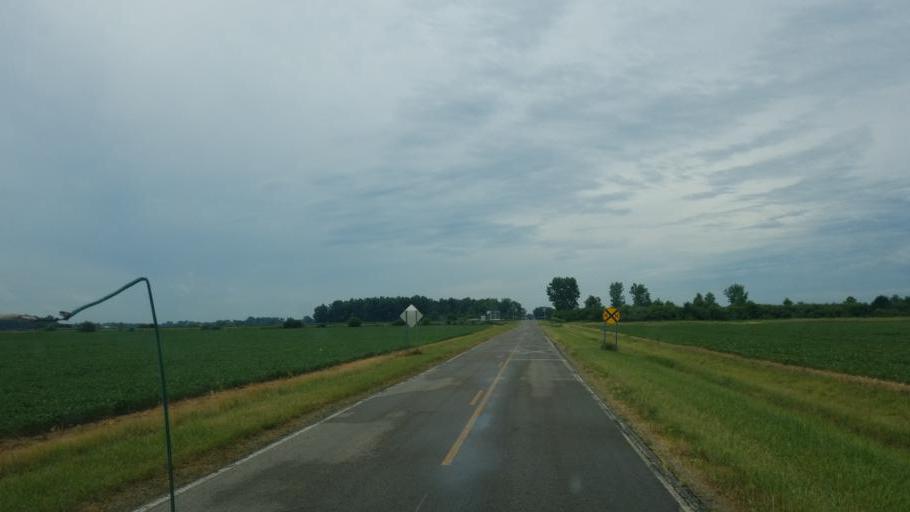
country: US
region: Ohio
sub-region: Defiance County
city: Hicksville
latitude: 41.2943
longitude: -84.6896
